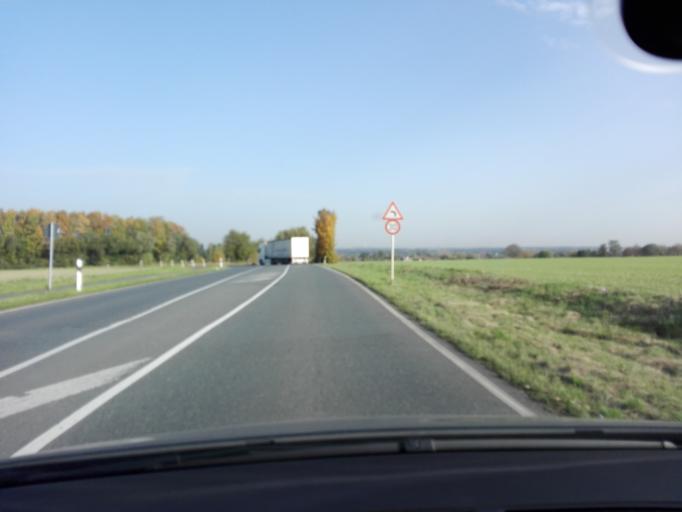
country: DE
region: North Rhine-Westphalia
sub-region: Regierungsbezirk Arnsberg
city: Holzwickede
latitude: 51.5272
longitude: 7.6343
